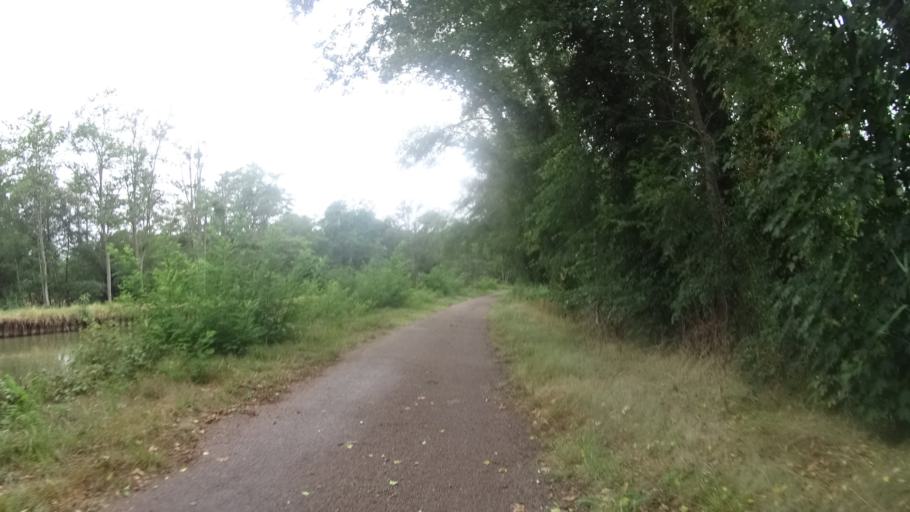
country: FR
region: Bourgogne
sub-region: Departement de la Nievre
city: Saint-Leger-des-Vignes
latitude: 46.8195
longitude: 3.4194
